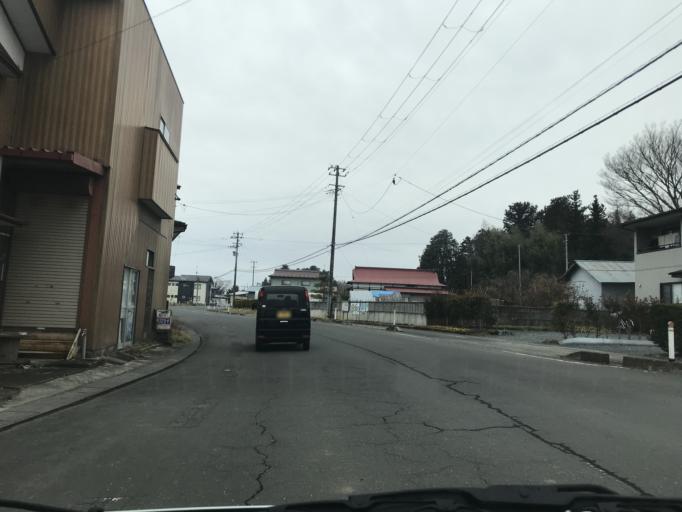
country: JP
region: Miyagi
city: Wakuya
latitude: 38.7243
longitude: 141.2153
